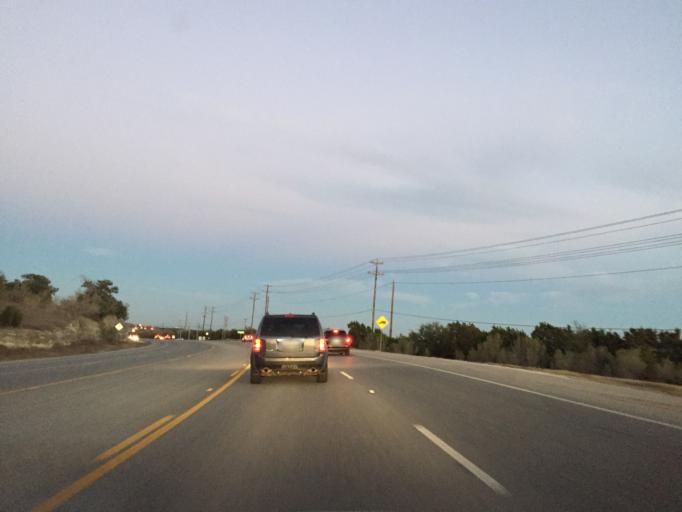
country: US
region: Texas
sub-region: Williamson County
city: Cedar Park
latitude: 30.5116
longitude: -97.8614
